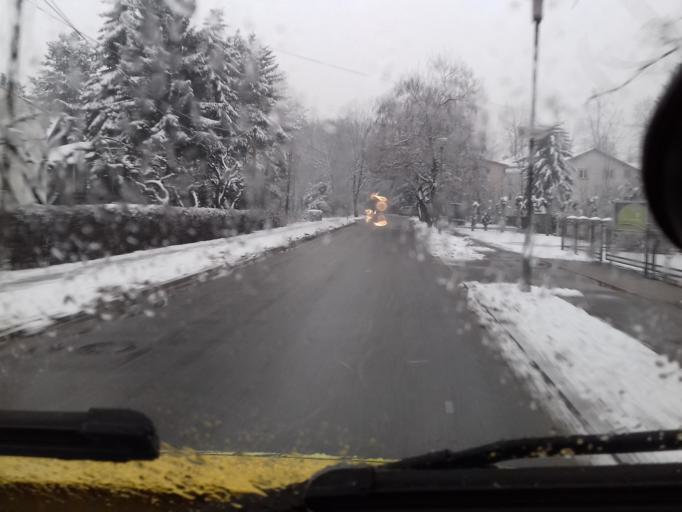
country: BA
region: Federation of Bosnia and Herzegovina
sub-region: Kanton Sarajevo
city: Sarajevo
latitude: 43.8254
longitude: 18.3007
